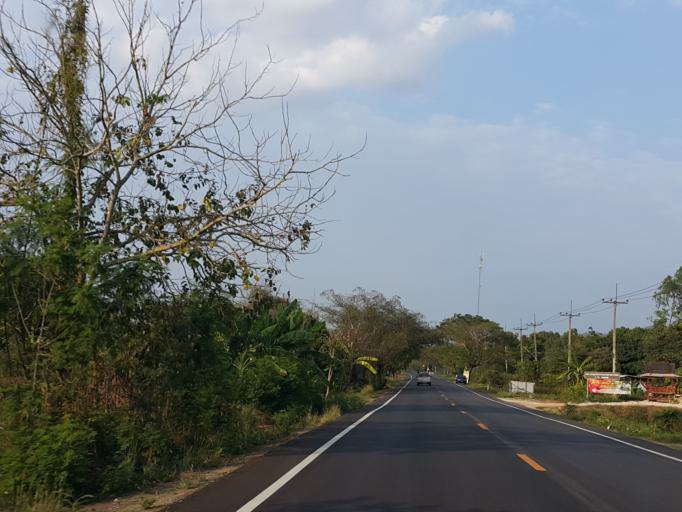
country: TH
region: Lampang
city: Lampang
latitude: 18.4765
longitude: 99.4685
